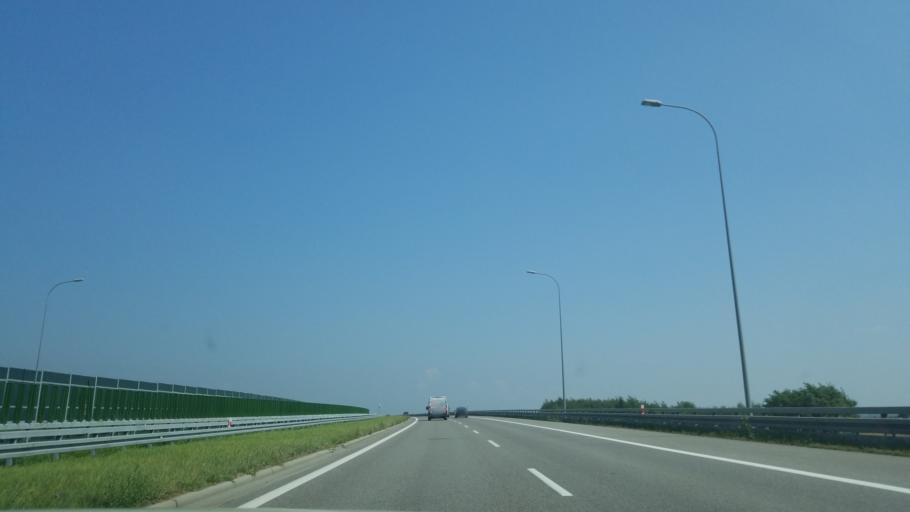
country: PL
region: Subcarpathian Voivodeship
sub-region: Powiat debicki
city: Brzeznica
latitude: 50.0798
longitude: 21.4790
